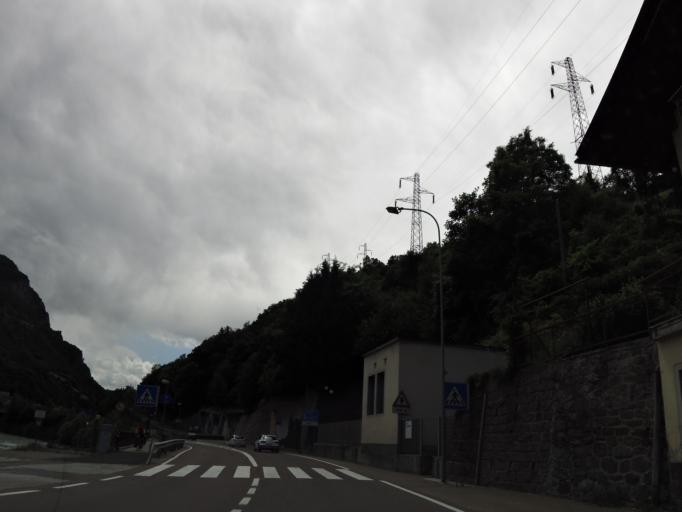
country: IT
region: Trentino-Alto Adige
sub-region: Bolzano
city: Ponte Gardena
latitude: 46.5984
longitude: 11.5291
